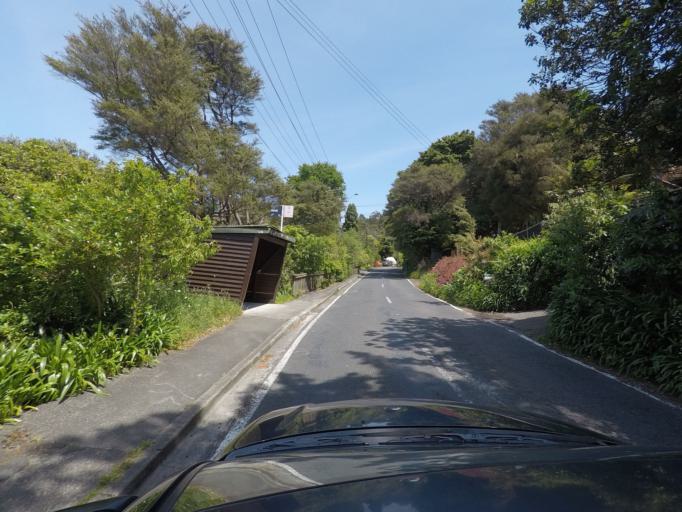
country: NZ
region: Auckland
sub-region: Auckland
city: Titirangi
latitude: -36.9649
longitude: 174.6399
